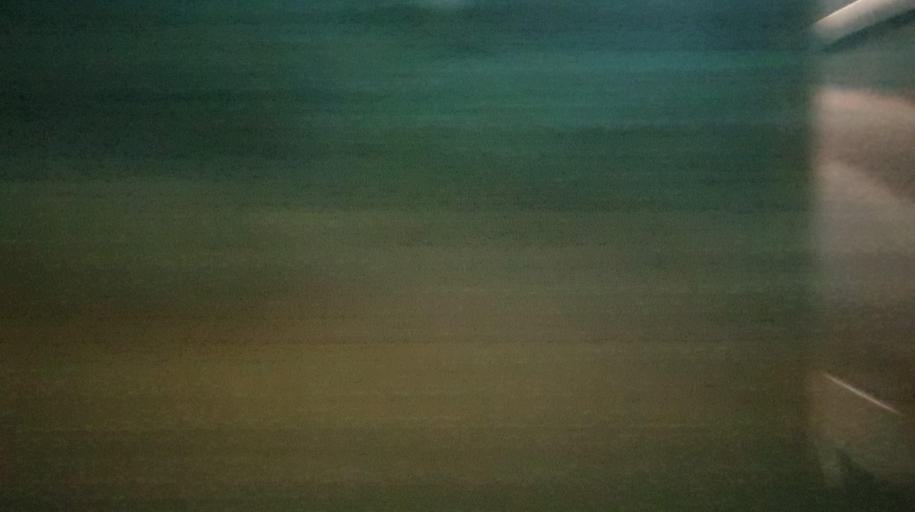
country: NO
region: Buskerud
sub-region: Drammen
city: Drammen
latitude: 59.7253
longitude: 10.2266
